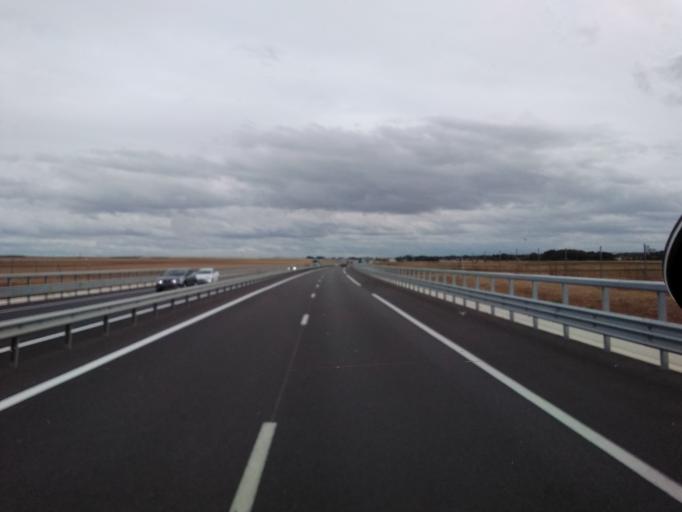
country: FR
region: Champagne-Ardenne
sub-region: Departement de la Marne
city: Sarry
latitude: 48.8992
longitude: 4.4496
